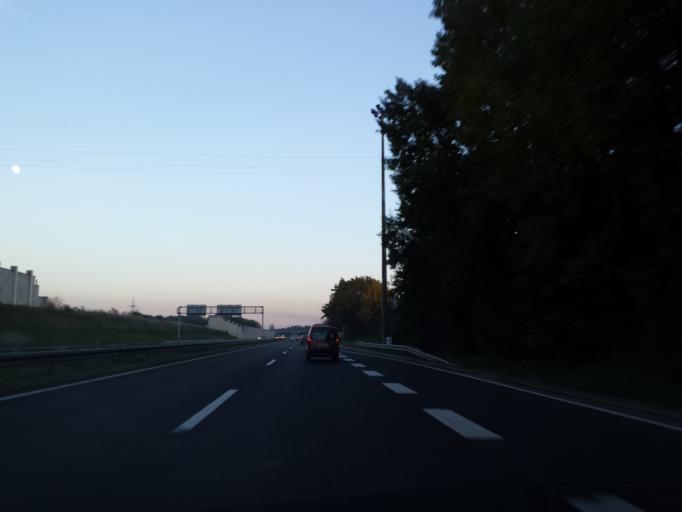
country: HR
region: Zagrebacka
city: Bestovje
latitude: 45.7959
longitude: 15.7876
